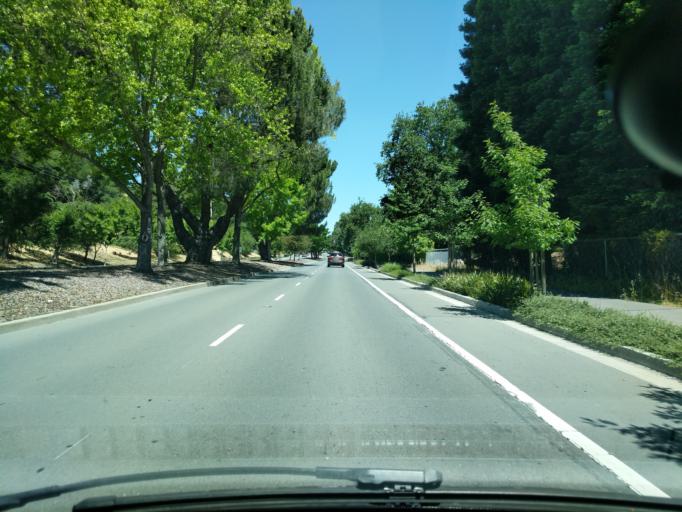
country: US
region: California
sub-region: Contra Costa County
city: Saranap
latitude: 37.8899
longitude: -122.0935
